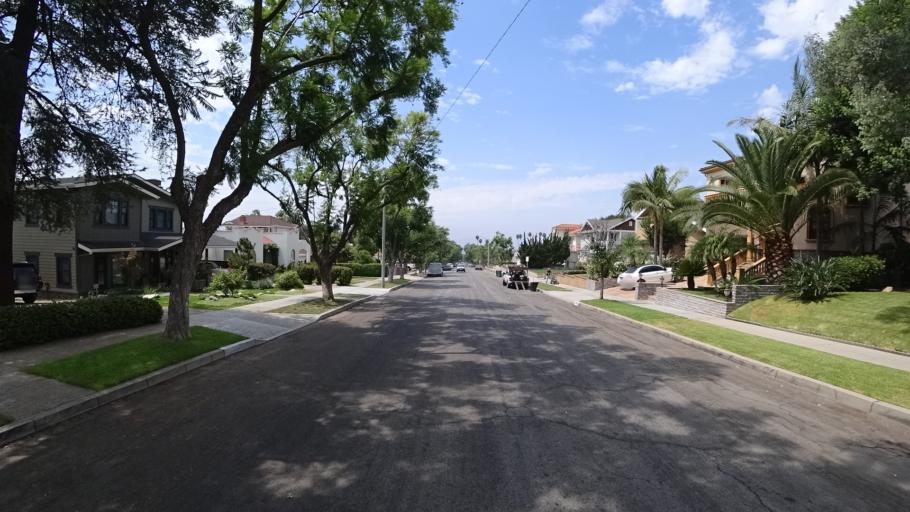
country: US
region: California
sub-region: Los Angeles County
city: Burbank
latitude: 34.1906
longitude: -118.2949
